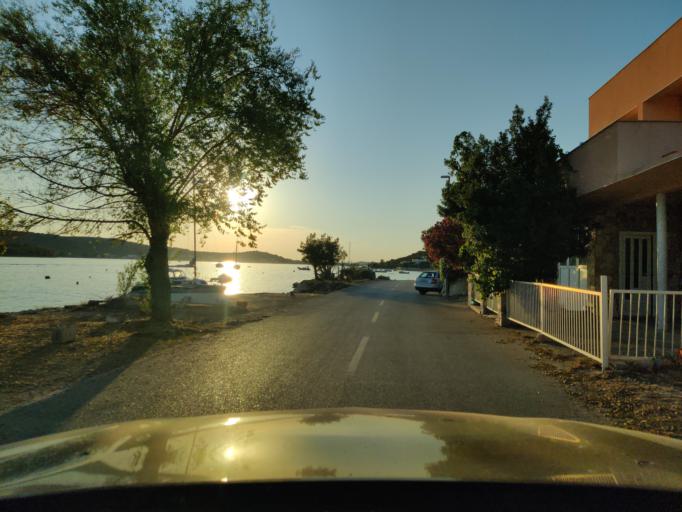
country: HR
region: Sibensko-Kniniska
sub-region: Grad Sibenik
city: Tisno
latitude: 43.8059
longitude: 15.6306
